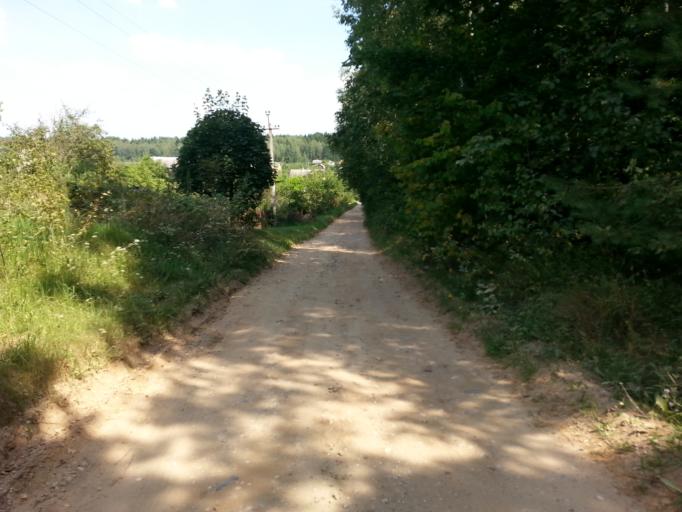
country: BY
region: Minsk
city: Pyatryshki
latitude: 54.0943
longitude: 27.1580
